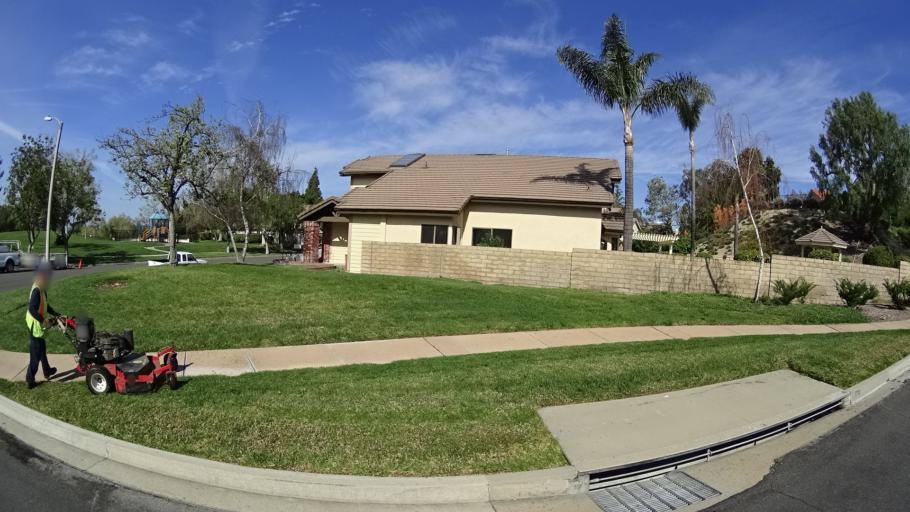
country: US
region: California
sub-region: Ventura County
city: Thousand Oaks
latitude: 34.2129
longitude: -118.8392
